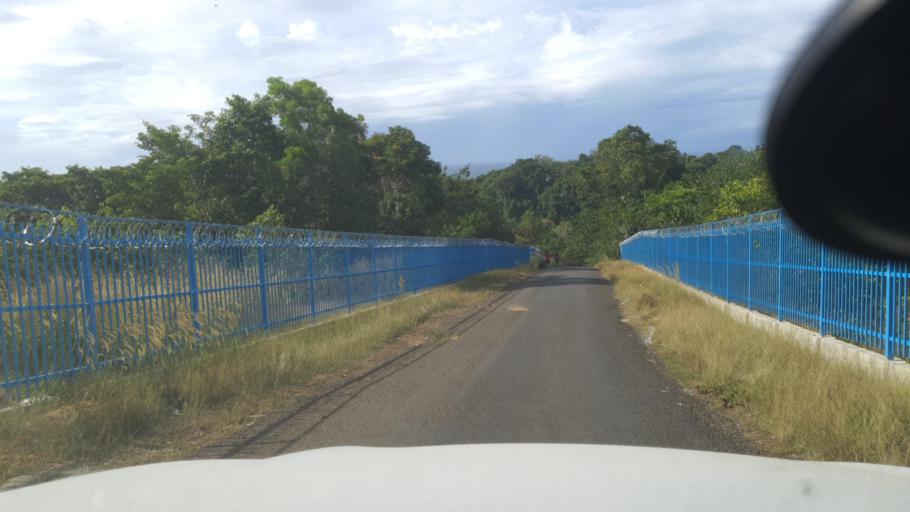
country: SB
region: Guadalcanal
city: Honiara
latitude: -9.4413
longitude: 159.9379
